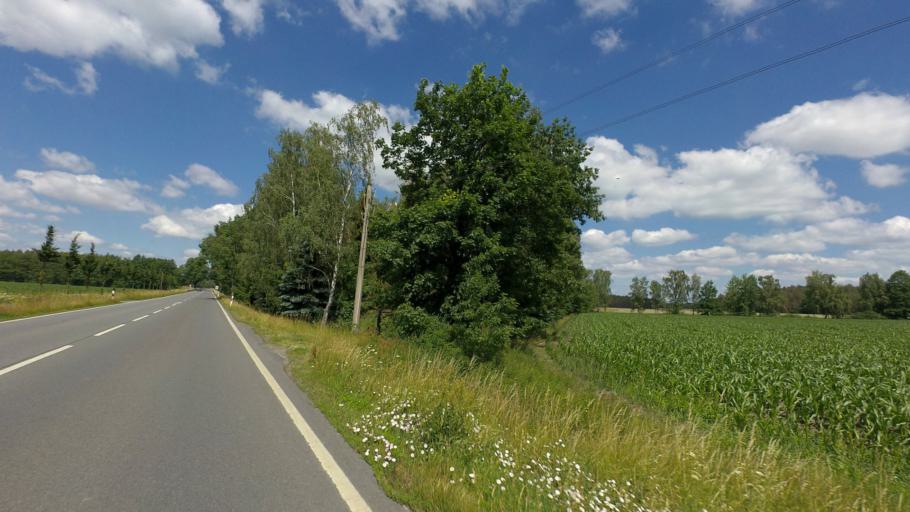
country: DE
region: Brandenburg
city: Finsterwalde
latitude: 51.6481
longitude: 13.6877
